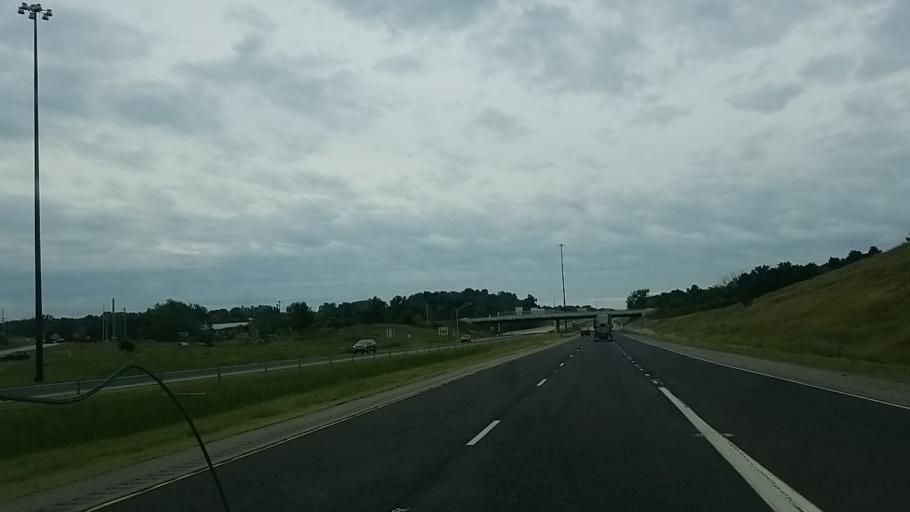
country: US
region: Indiana
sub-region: Steuben County
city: Angola
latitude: 41.7037
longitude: -85.0049
